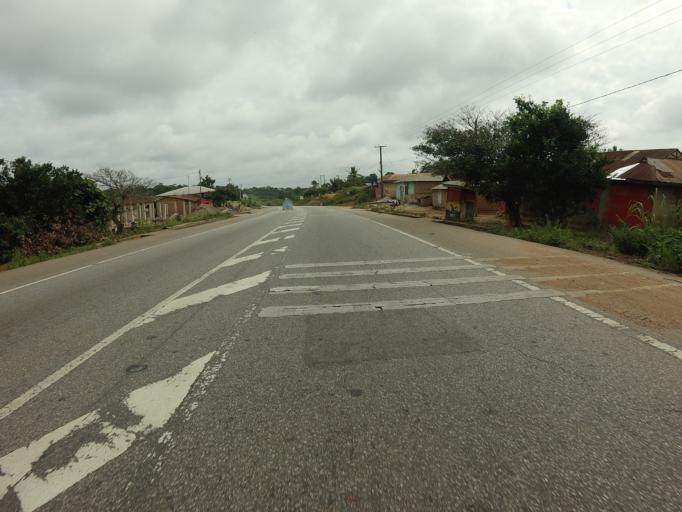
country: GH
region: Ashanti
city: Mampong
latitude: 7.0379
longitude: -1.7081
